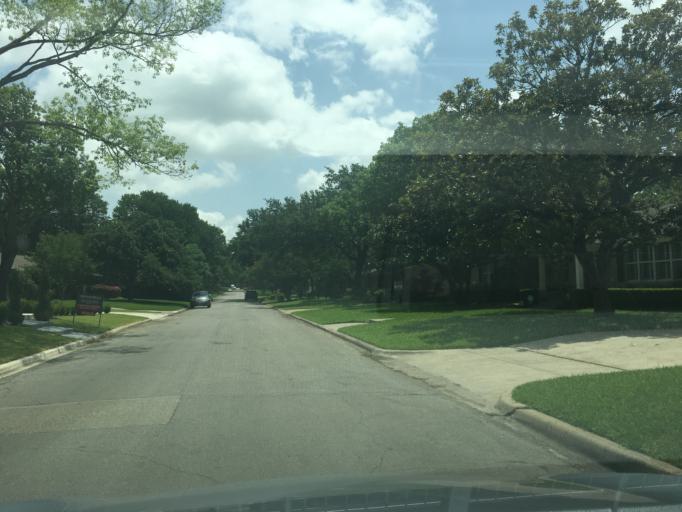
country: US
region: Texas
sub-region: Dallas County
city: University Park
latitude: 32.8790
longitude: -96.7933
